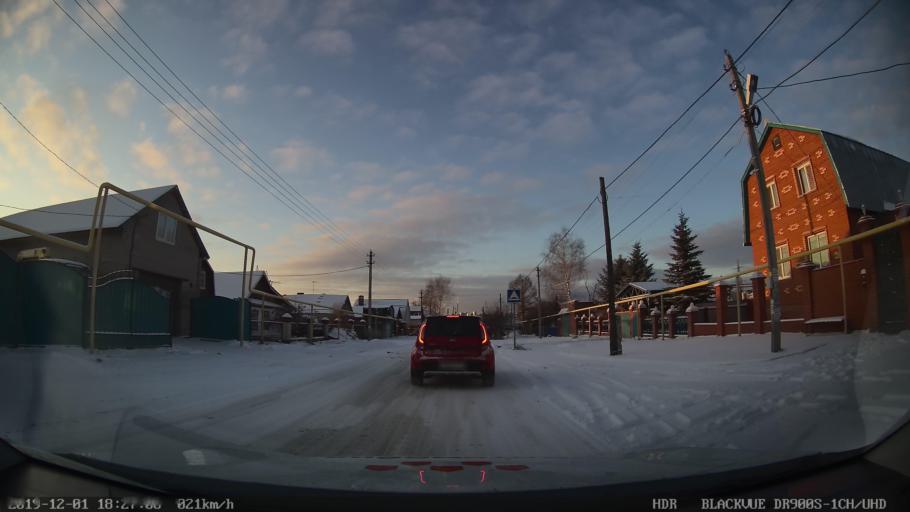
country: RU
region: Tatarstan
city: Vysokaya Gora
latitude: 55.8054
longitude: 49.2547
